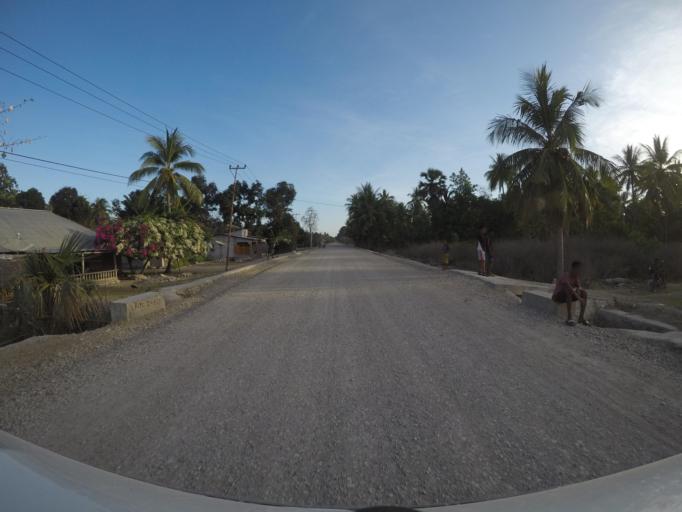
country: TL
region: Viqueque
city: Viqueque
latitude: -8.8509
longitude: 126.5125
